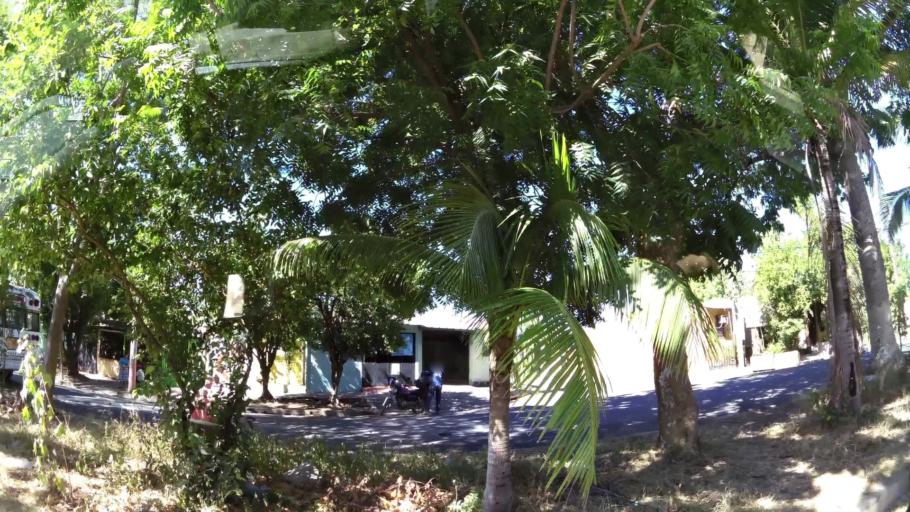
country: SV
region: San Miguel
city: San Miguel
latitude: 13.4943
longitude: -88.1647
